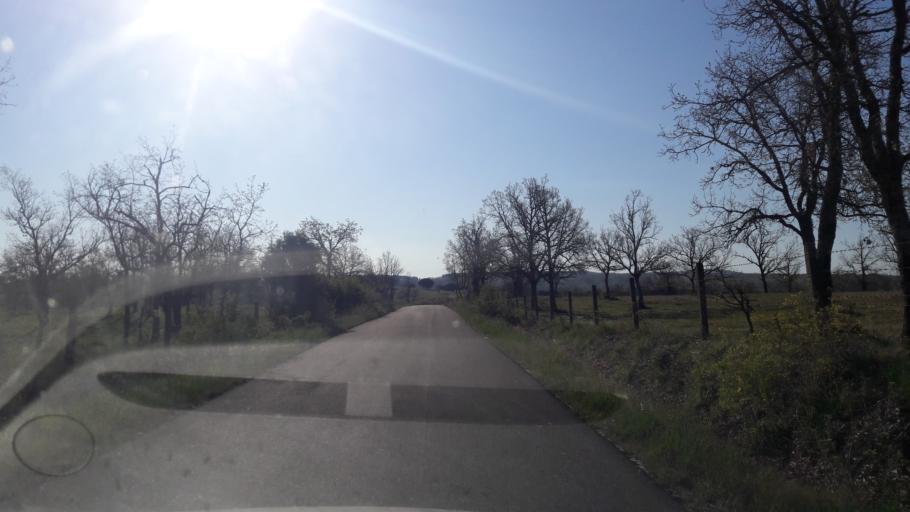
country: ES
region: Castille and Leon
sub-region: Provincia de Salamanca
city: Monleon
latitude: 40.6058
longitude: -5.8406
